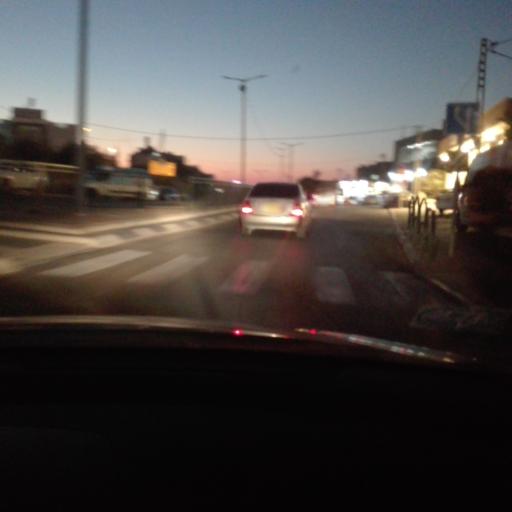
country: PS
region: West Bank
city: Nazlat `Isa
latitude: 32.4232
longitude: 35.0379
